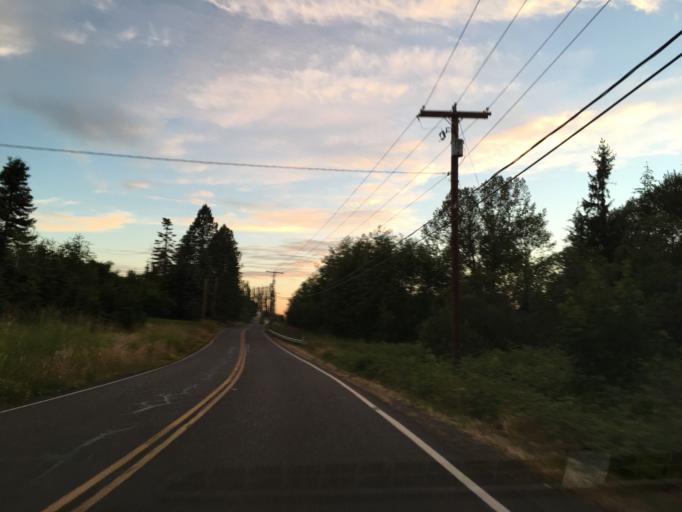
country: US
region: Washington
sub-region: Whatcom County
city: Bellingham
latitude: 48.7859
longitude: -122.4709
